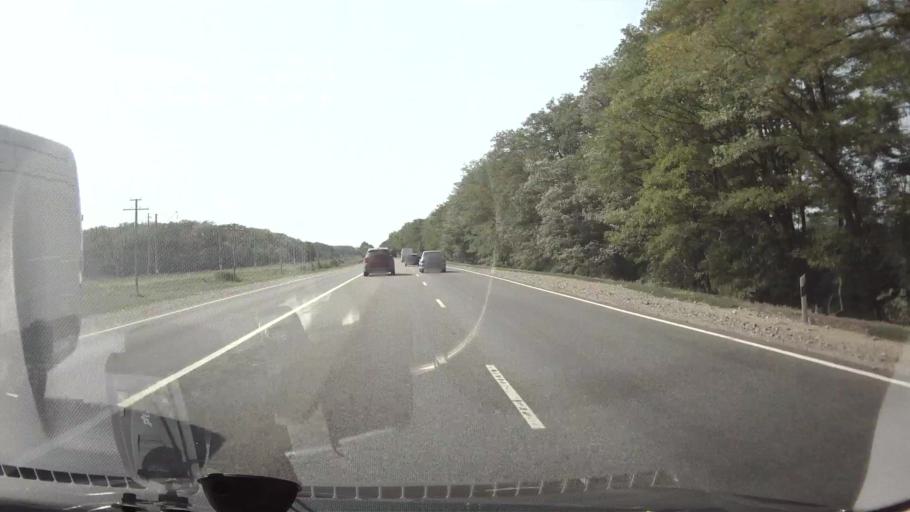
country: RU
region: Krasnodarskiy
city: Dvubratskiy
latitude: 45.2717
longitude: 39.8147
